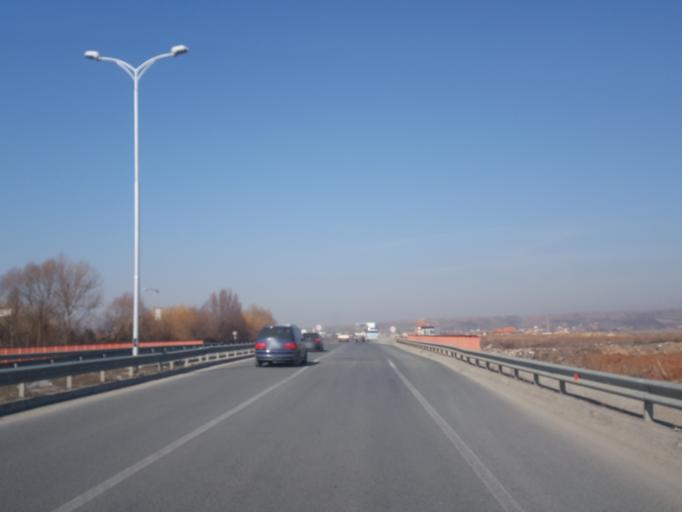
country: XK
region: Pristina
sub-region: Komuna e Obiliqit
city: Obiliq
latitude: 42.7264
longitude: 21.0791
